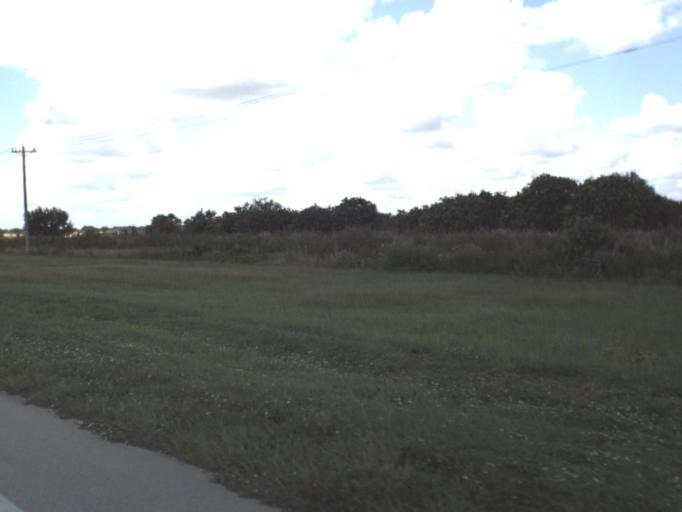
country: US
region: Florida
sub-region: Lee County
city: Lehigh Acres
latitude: 26.5139
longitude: -81.5458
